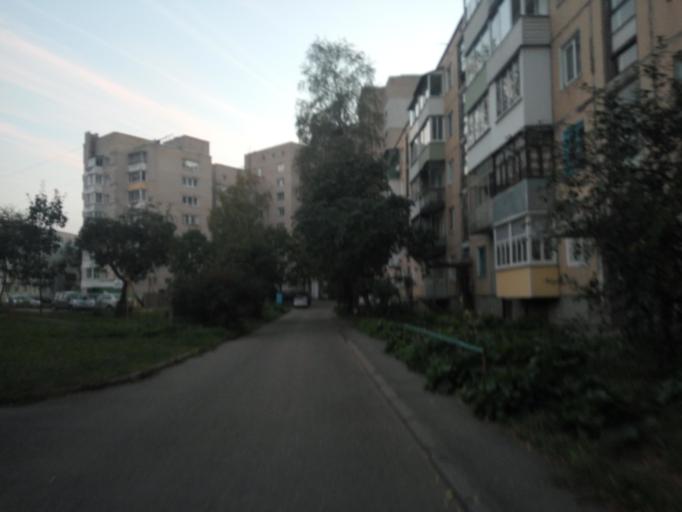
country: BY
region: Vitebsk
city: Vitebsk
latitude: 55.2009
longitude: 30.2411
